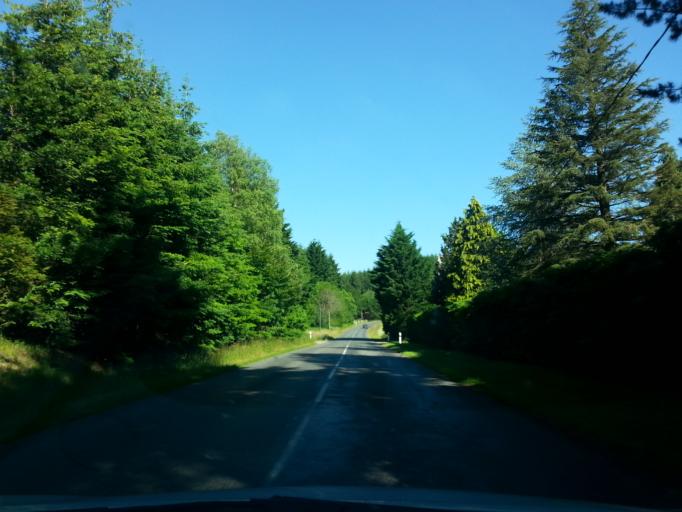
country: FR
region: Rhone-Alpes
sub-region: Departement de la Loire
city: Belmont-de-la-Loire
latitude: 46.1760
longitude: 4.4230
